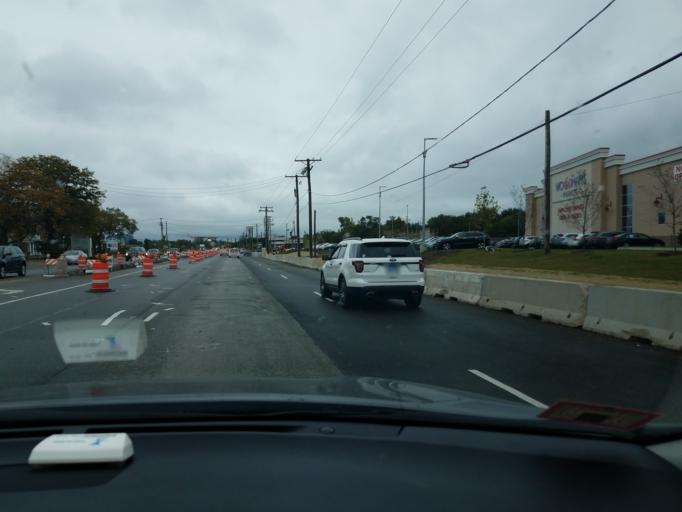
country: US
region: Illinois
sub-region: Lake County
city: Lincolnshire
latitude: 42.1696
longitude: -87.9224
